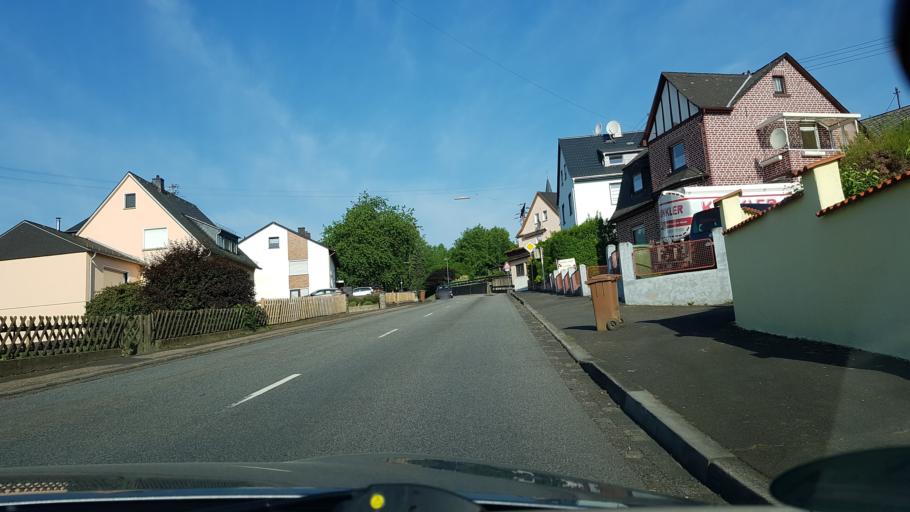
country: DE
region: Rheinland-Pfalz
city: Kadenbach
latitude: 50.3845
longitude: 7.7291
